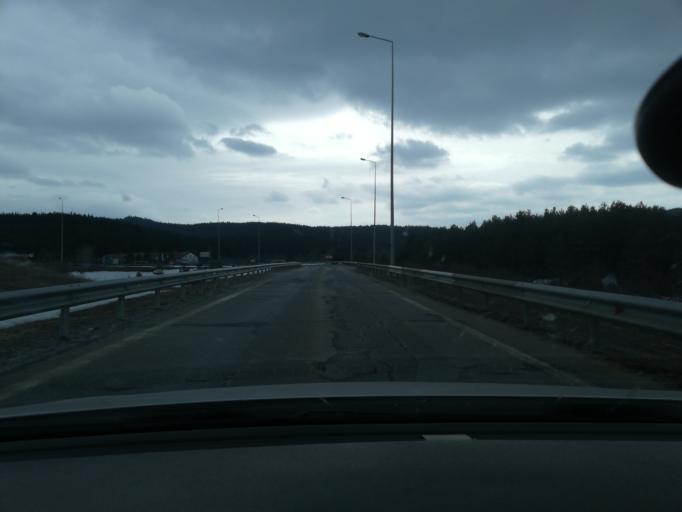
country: TR
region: Bolu
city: Gerede
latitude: 40.6113
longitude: 32.2510
